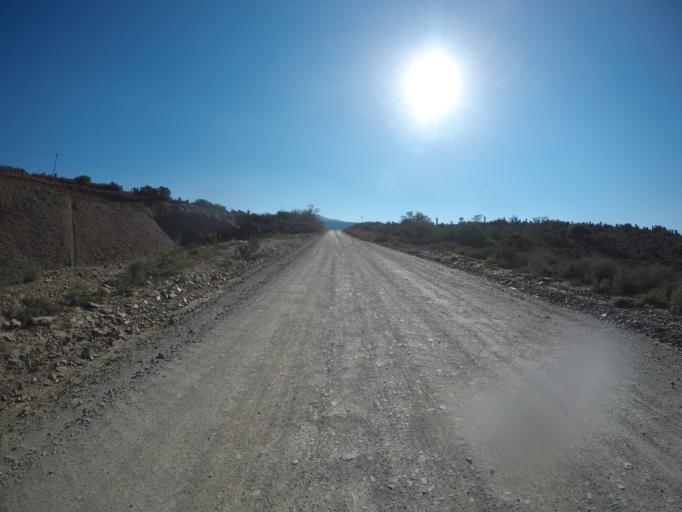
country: ZA
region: Eastern Cape
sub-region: Cacadu District Municipality
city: Kruisfontein
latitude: -33.6733
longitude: 24.5762
